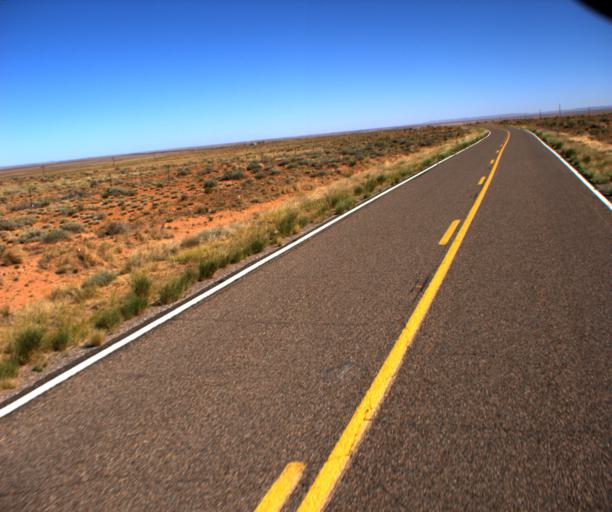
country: US
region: Arizona
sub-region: Coconino County
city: LeChee
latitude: 35.1041
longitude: -110.8641
